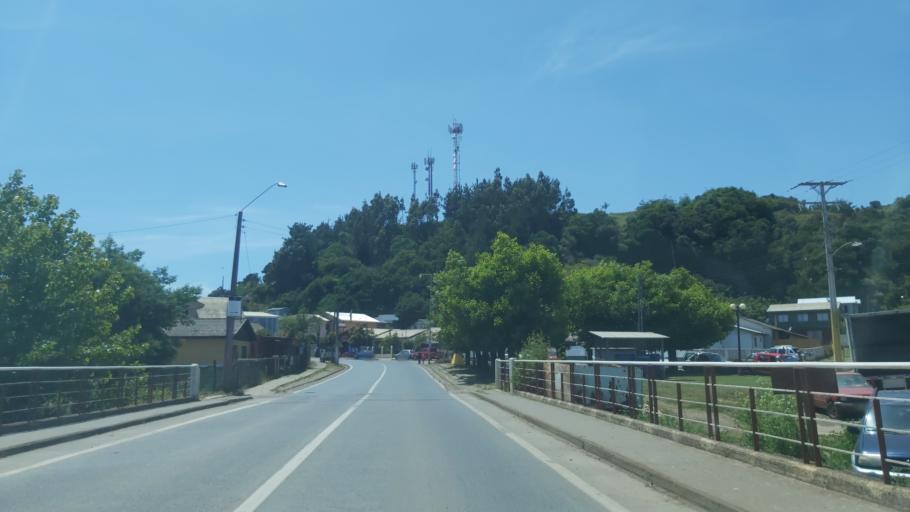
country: CL
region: Maule
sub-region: Provincia de Cauquenes
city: Cauquenes
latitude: -35.8433
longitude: -72.6310
